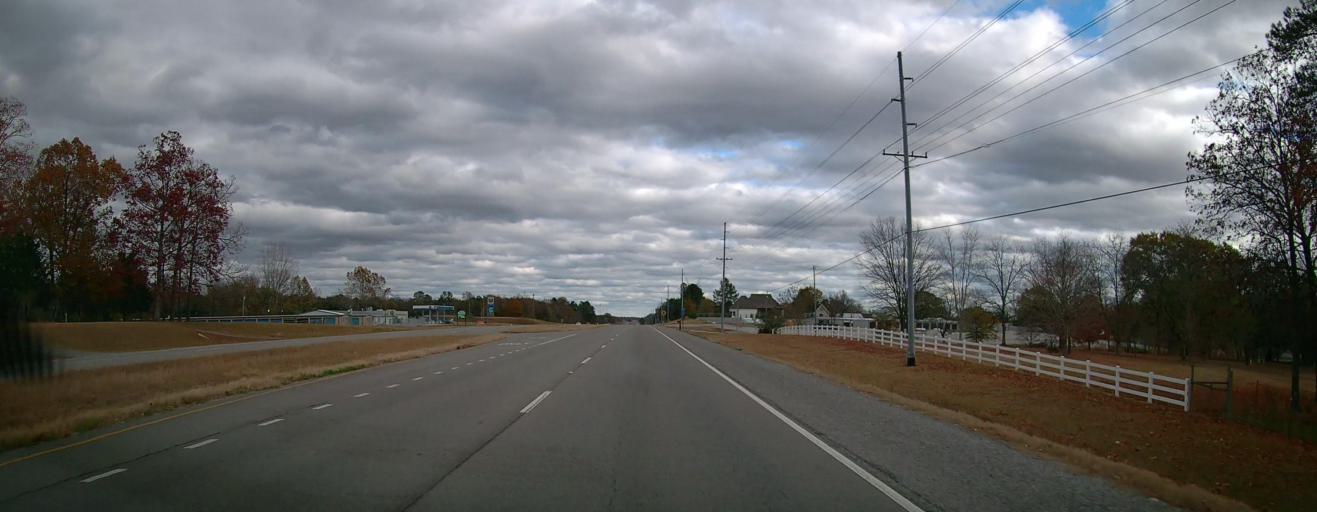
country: US
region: Alabama
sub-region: Lawrence County
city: Town Creek
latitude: 34.5678
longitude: -87.3747
